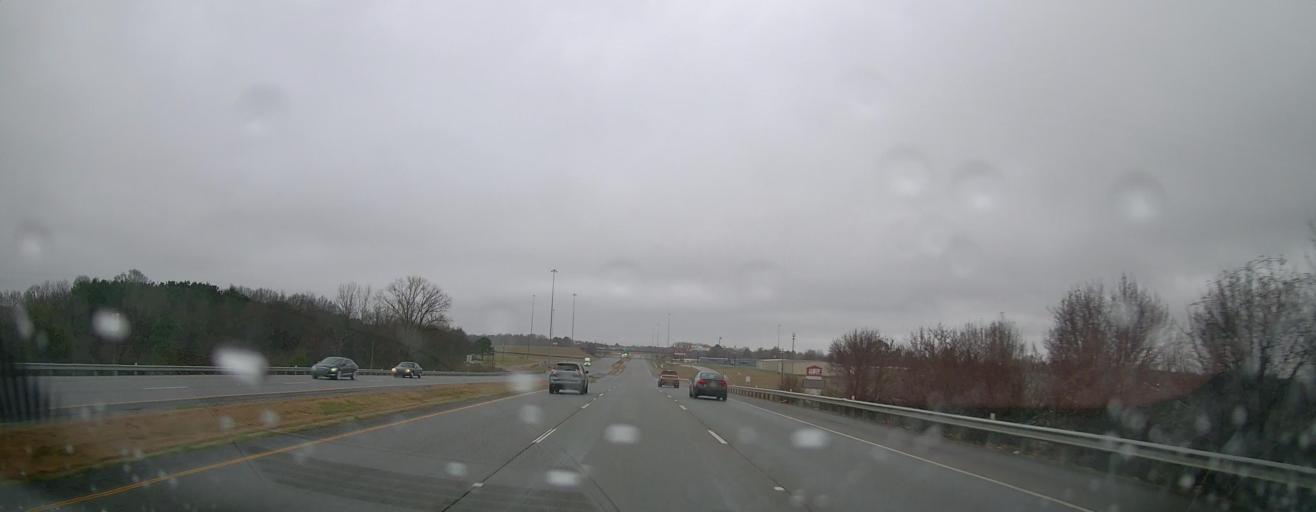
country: US
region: Alabama
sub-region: Morgan County
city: Decatur
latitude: 34.6086
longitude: -87.0312
